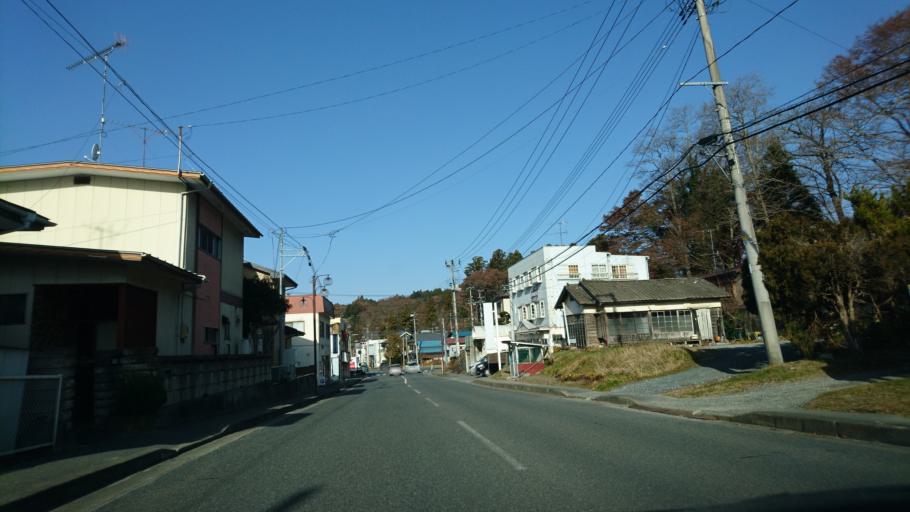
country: JP
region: Iwate
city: Ichinoseki
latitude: 38.9185
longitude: 141.3394
